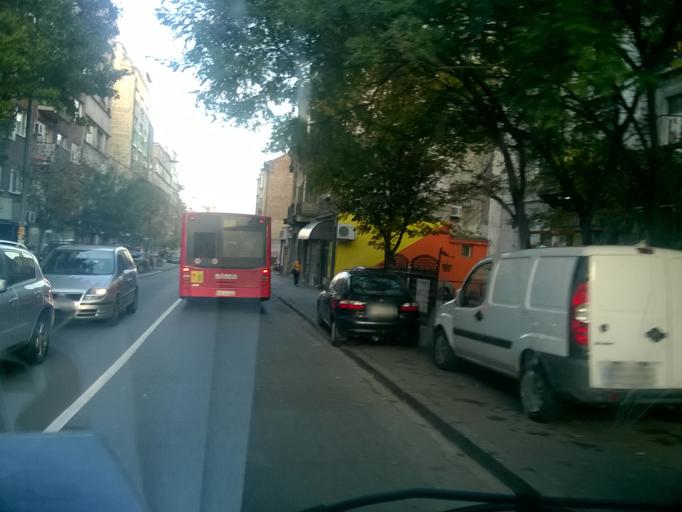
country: RS
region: Central Serbia
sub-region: Belgrade
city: Stari Grad
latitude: 44.8167
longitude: 20.4670
